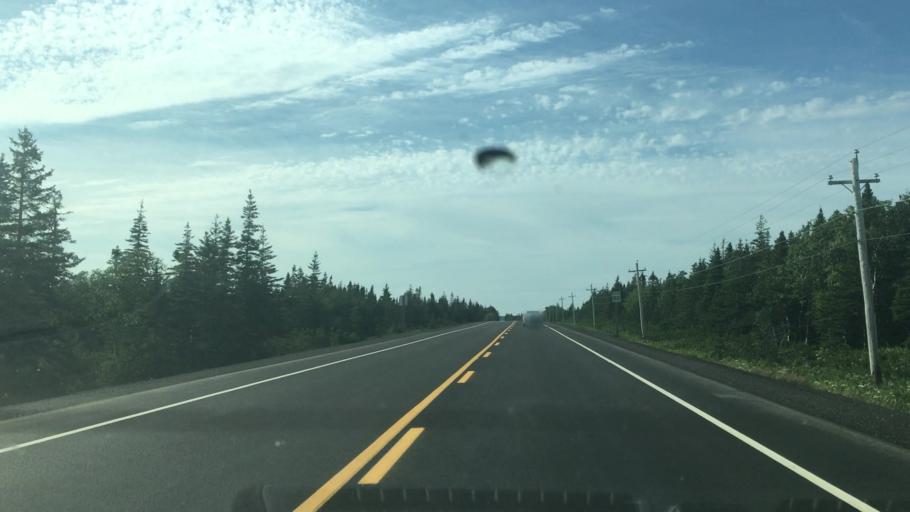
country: CA
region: Nova Scotia
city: Sydney Mines
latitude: 46.8459
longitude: -60.4102
